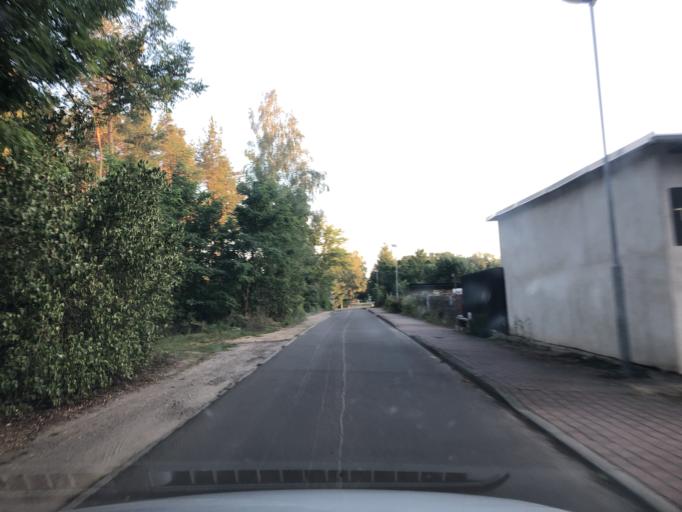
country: DE
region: Brandenburg
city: Mullrose
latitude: 52.2476
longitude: 14.4765
